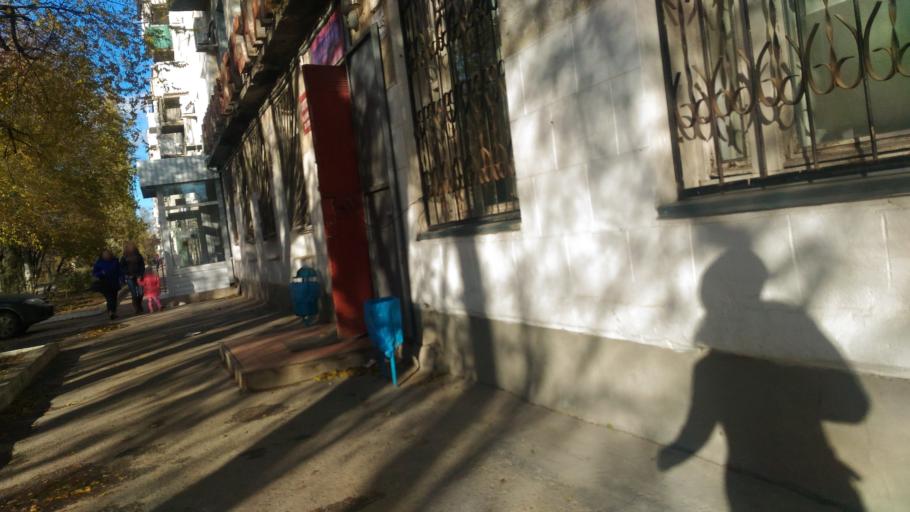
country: RU
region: Volgograd
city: Volgograd
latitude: 48.6073
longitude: 44.4229
